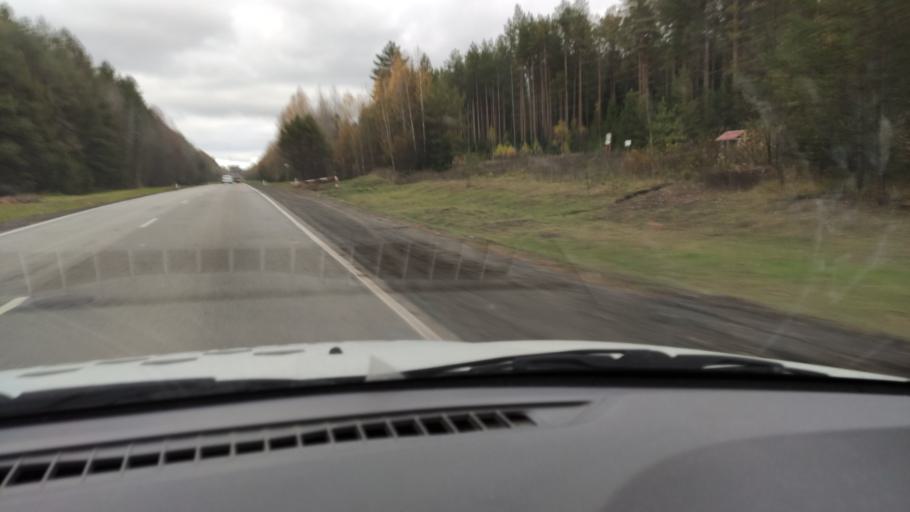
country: RU
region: Kirov
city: Belaya Kholunitsa
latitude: 58.7915
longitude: 50.5174
